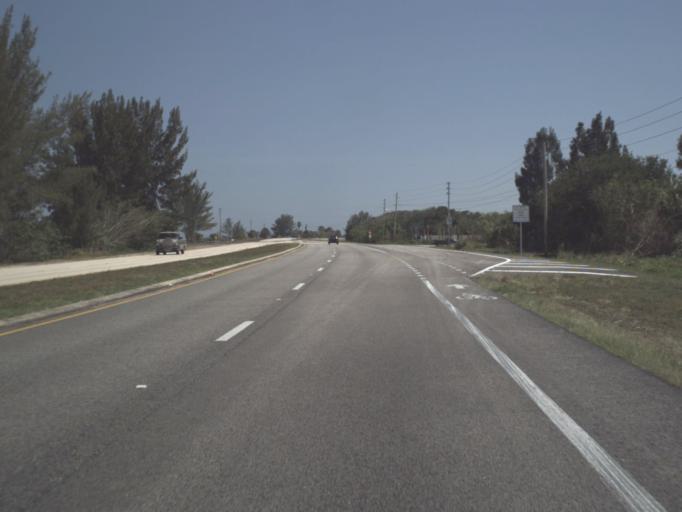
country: US
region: Florida
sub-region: Brevard County
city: Grant-Valkaria
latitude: 27.9654
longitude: -80.5427
